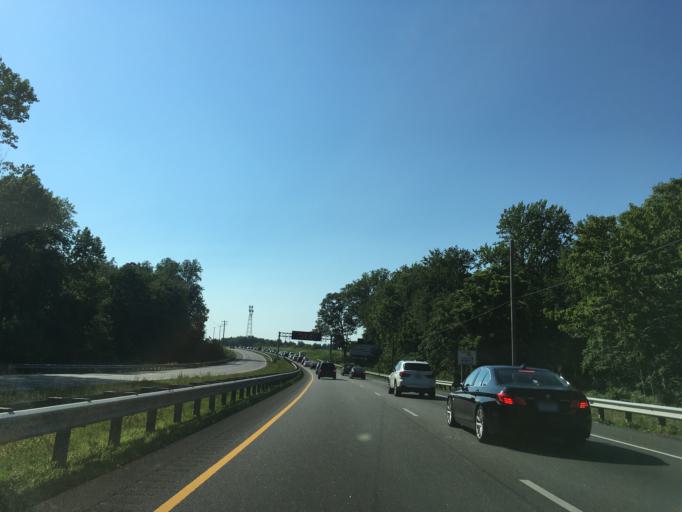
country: US
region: Maryland
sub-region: Queen Anne's County
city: Centreville
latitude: 38.9494
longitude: -76.0664
